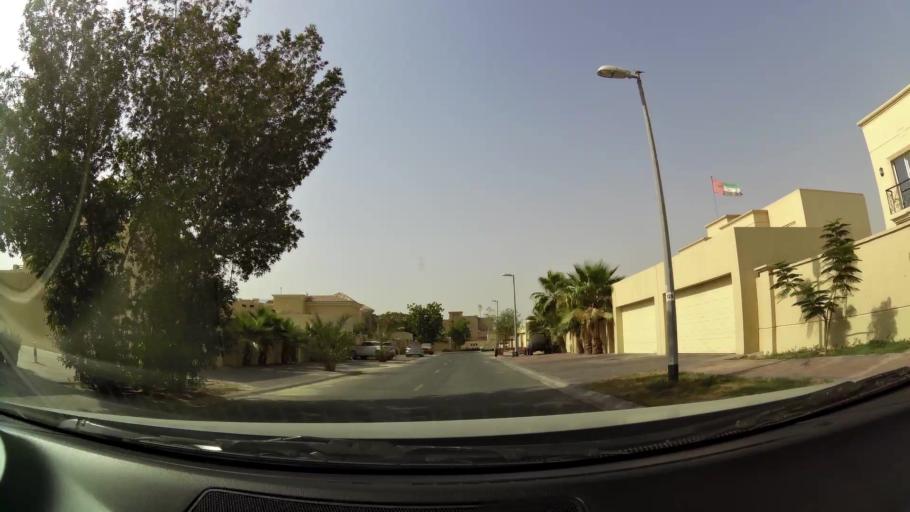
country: AE
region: Ash Shariqah
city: Sharjah
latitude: 25.2666
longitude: 55.4540
